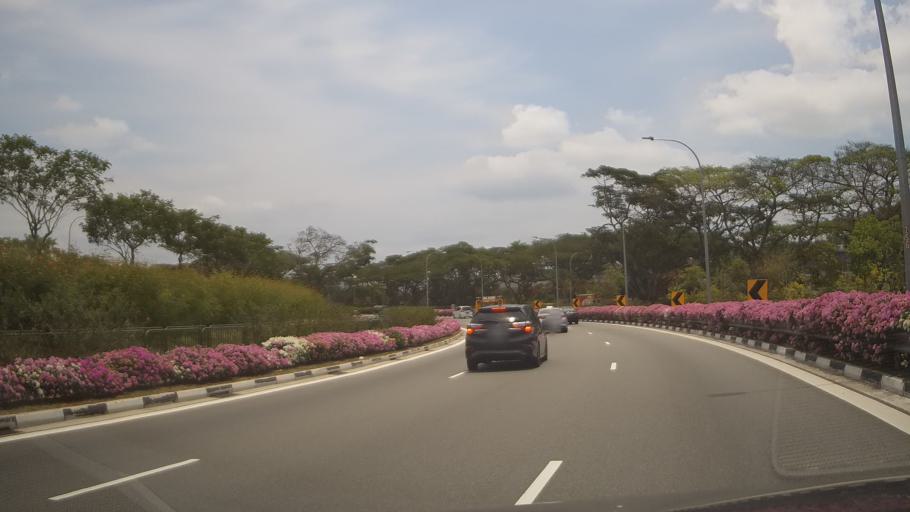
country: SG
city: Singapore
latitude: 1.3377
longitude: 103.9793
